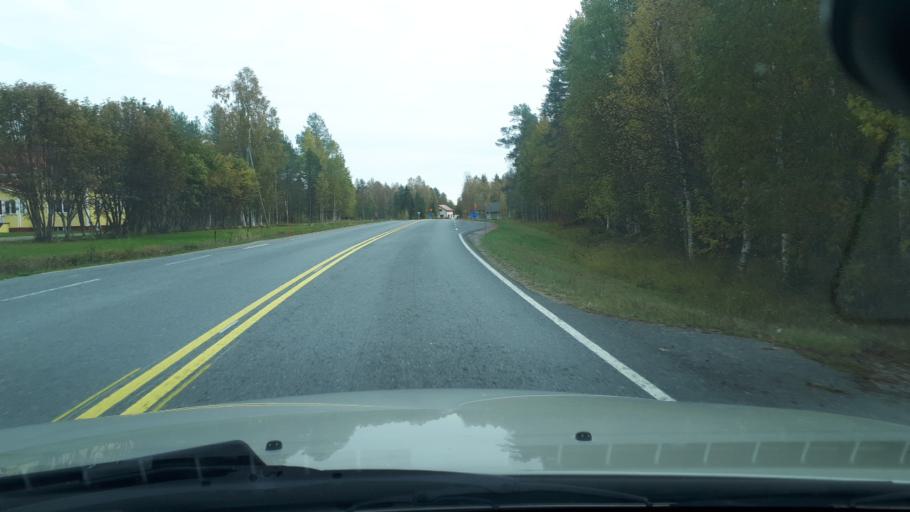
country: FI
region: Lapland
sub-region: Rovaniemi
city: Ranua
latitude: 66.0130
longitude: 26.3149
